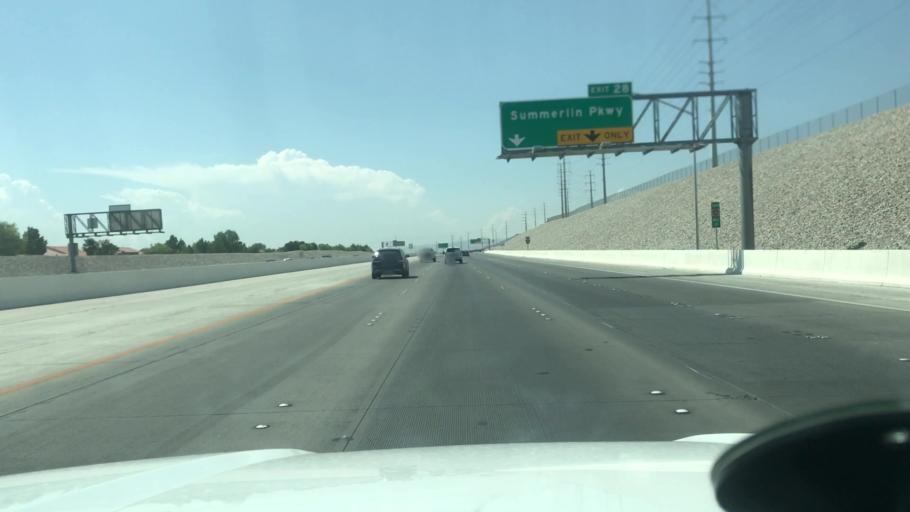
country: US
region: Nevada
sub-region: Clark County
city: Summerlin South
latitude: 36.2015
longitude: -115.3415
